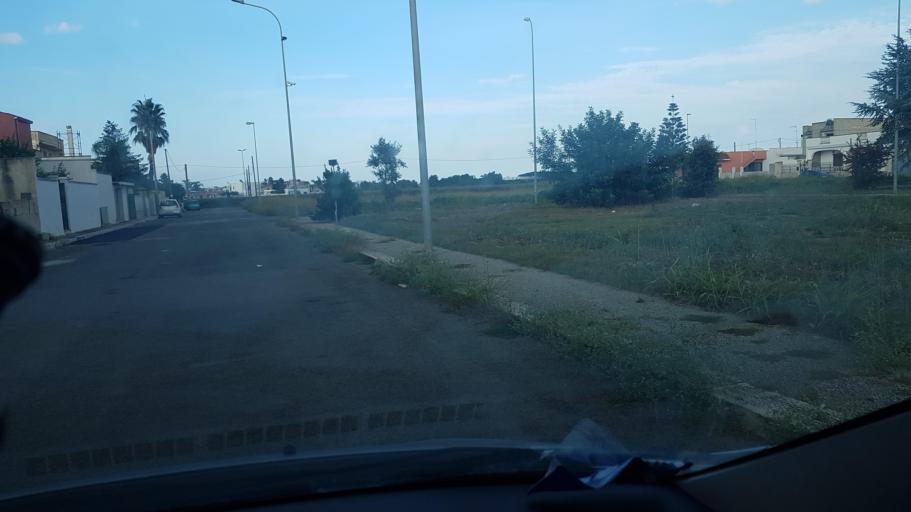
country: IT
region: Apulia
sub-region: Provincia di Brindisi
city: Cellino San Marco
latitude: 40.4691
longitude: 17.9725
